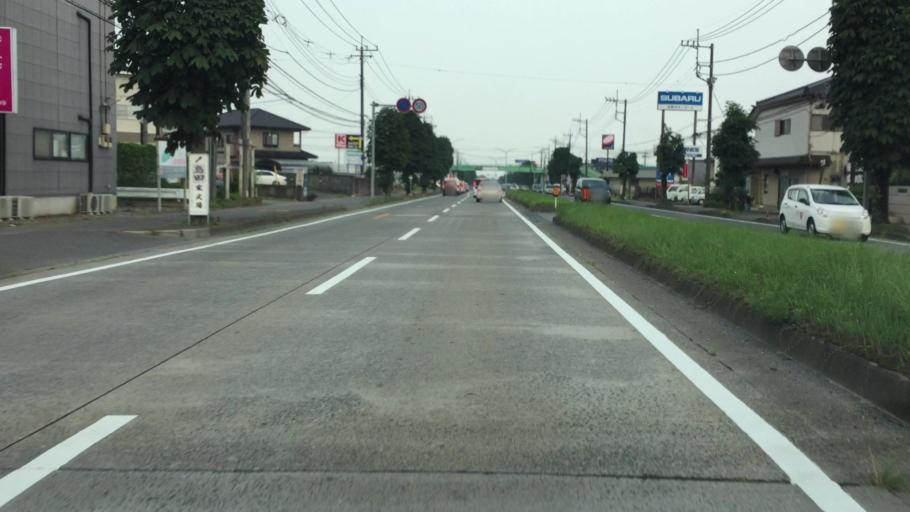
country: JP
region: Tochigi
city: Tochigi
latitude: 36.4000
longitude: 139.7163
